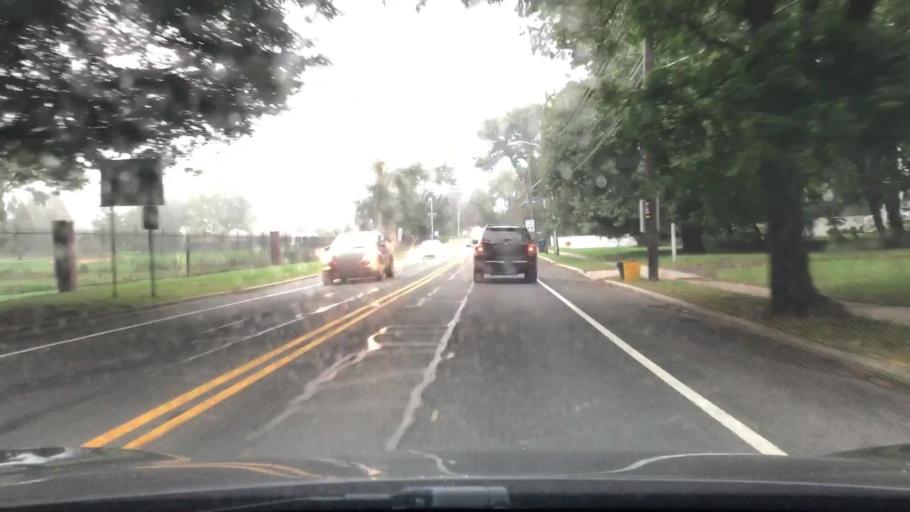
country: US
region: New Jersey
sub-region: Mercer County
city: Lawrenceville
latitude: 40.3006
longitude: -74.7269
